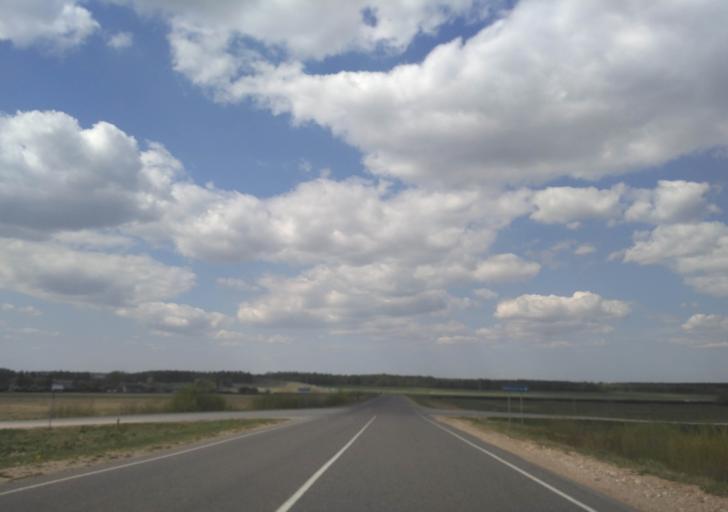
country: BY
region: Minsk
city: Vilyeyka
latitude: 54.5188
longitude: 26.9761
